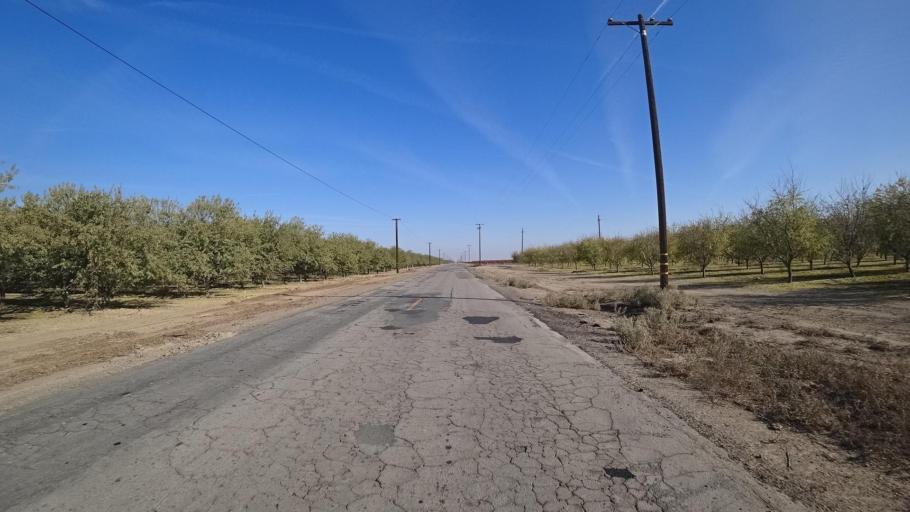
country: US
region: California
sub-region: Kern County
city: Wasco
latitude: 35.7032
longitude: -119.3806
